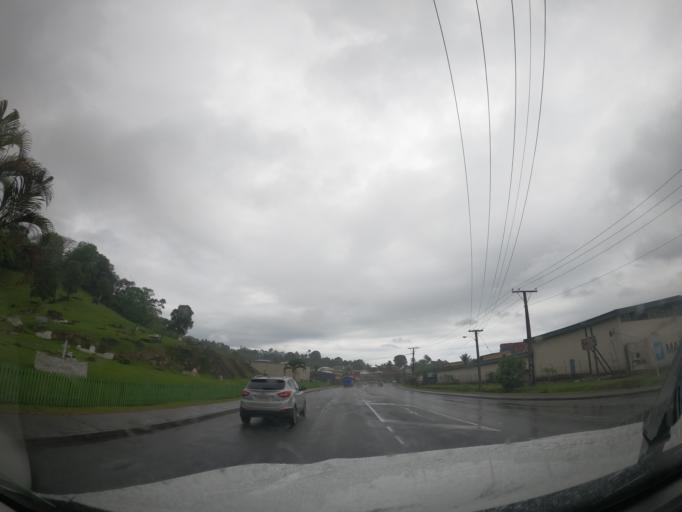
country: FJ
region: Central
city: Suva
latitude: -18.1180
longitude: 178.4311
